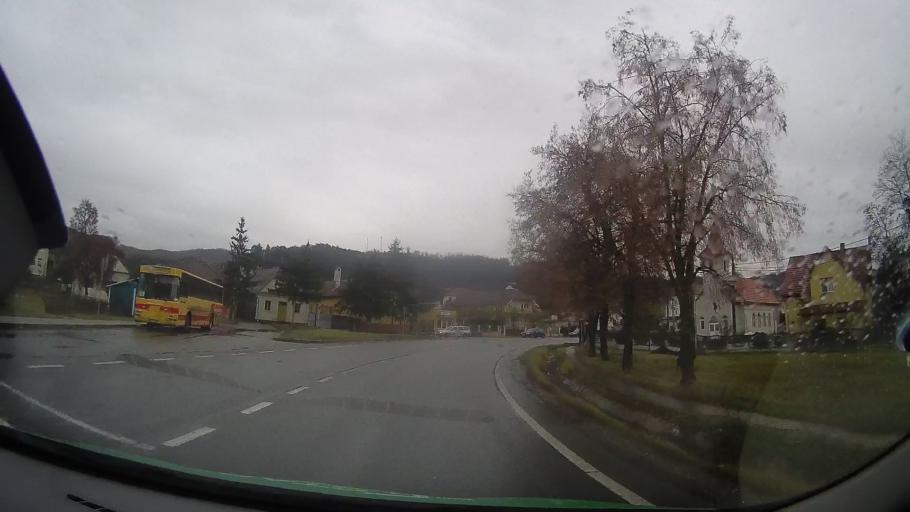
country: RO
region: Bistrita-Nasaud
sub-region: Comuna Teaca
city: Teaca
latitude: 46.9111
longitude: 24.5071
